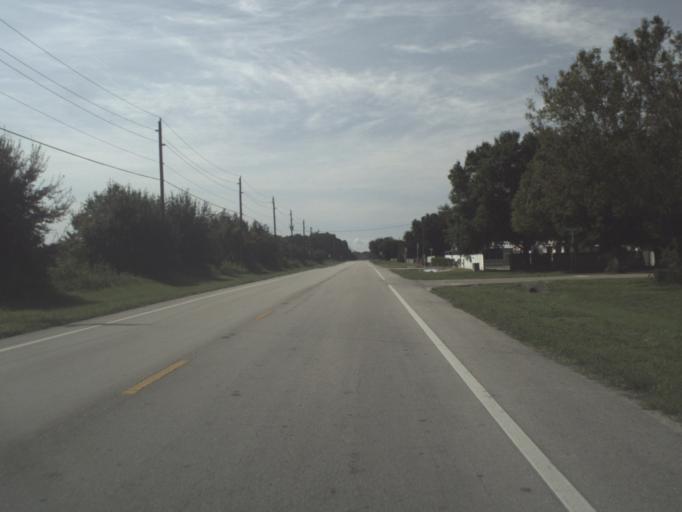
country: US
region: Florida
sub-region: DeSoto County
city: Southeast Arcadia
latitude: 27.1926
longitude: -81.8280
